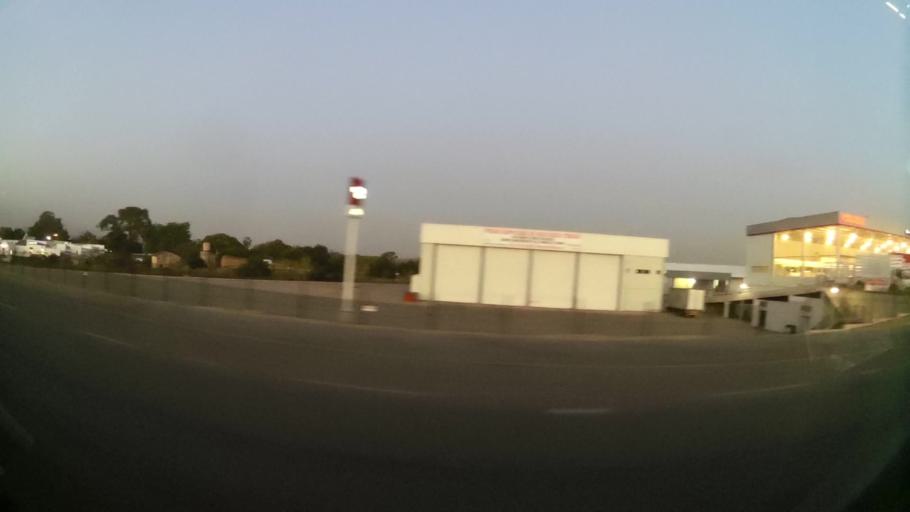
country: ZA
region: North-West
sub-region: Bojanala Platinum District Municipality
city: Rustenburg
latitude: -25.6841
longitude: 27.2548
